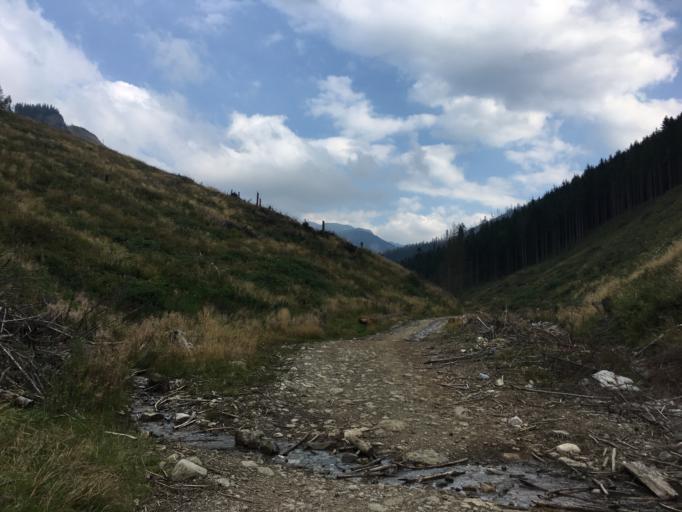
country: PL
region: Lesser Poland Voivodeship
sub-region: Powiat tatrzanski
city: Koscielisko
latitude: 49.2627
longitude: 19.8458
